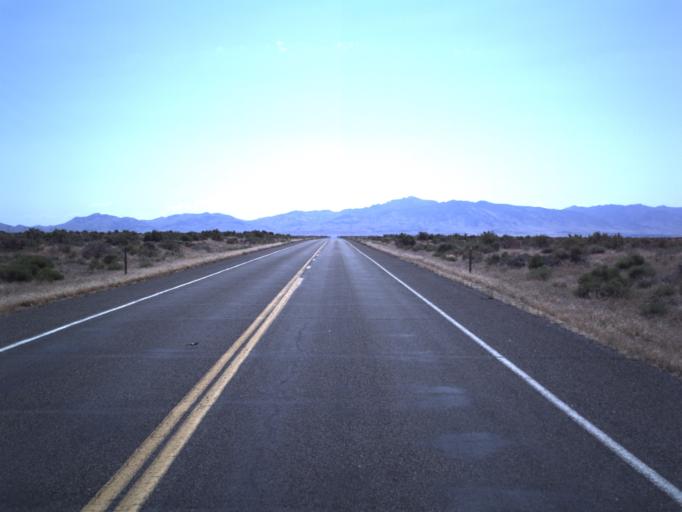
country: US
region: Utah
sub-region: Millard County
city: Delta
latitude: 39.4897
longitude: -112.5542
